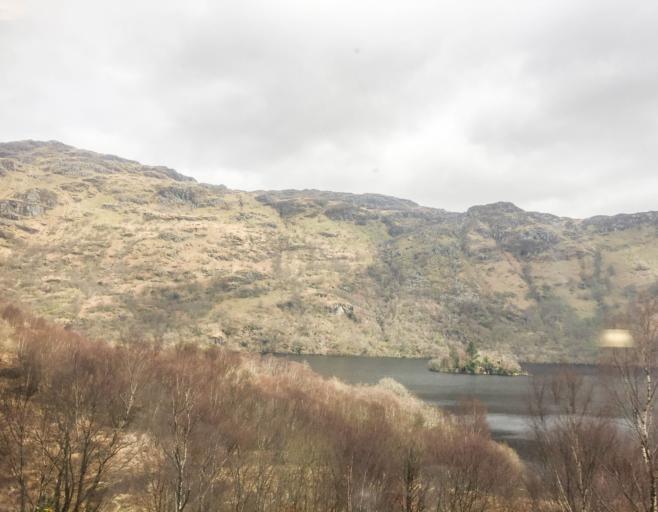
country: GB
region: Scotland
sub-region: Argyll and Bute
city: Garelochhead
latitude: 56.2792
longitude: -4.7062
